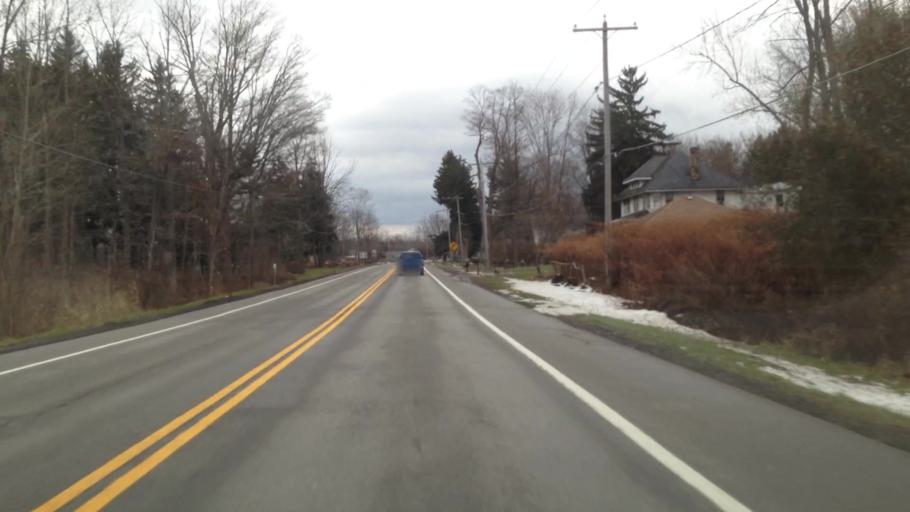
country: US
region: New York
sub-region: Erie County
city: Akron
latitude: 42.9980
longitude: -78.4666
